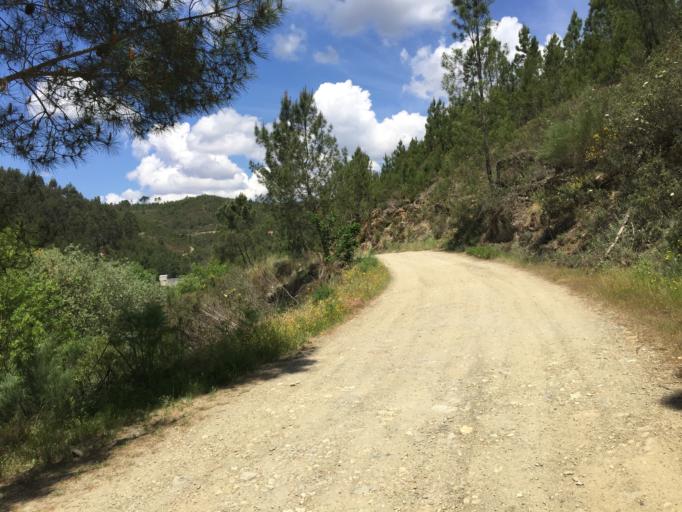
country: PT
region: Coimbra
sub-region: Pampilhosa da Serra
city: Pampilhosa da Serra
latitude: 40.0777
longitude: -7.7875
